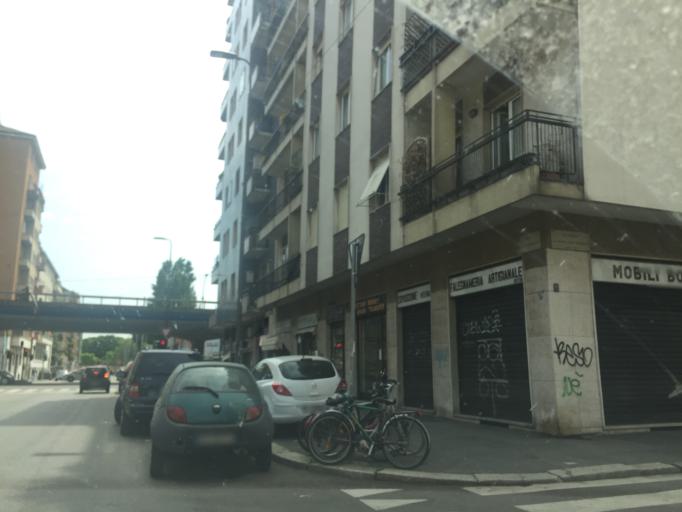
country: IT
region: Lombardy
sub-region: Citta metropolitana di Milano
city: Novate Milanese
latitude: 45.4930
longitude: 9.1546
